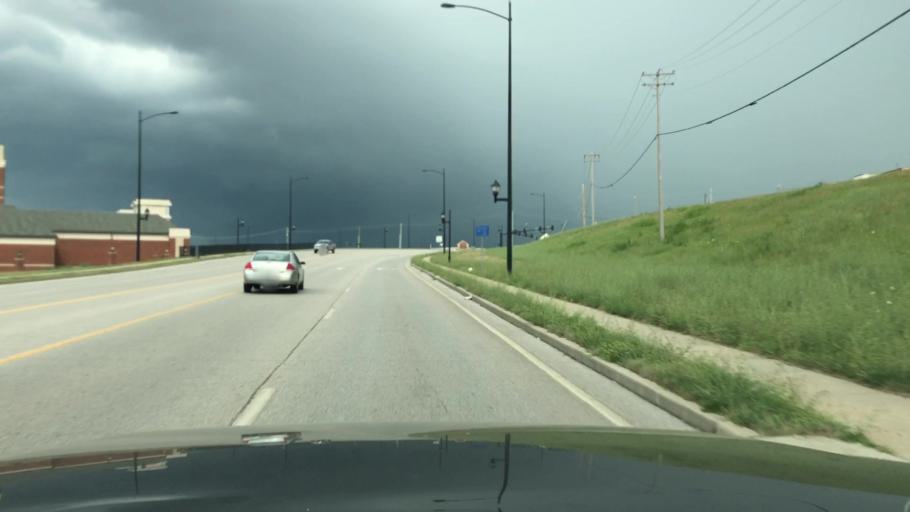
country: US
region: Missouri
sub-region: Saint Charles County
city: Saint Charles
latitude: 38.7835
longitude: -90.5075
